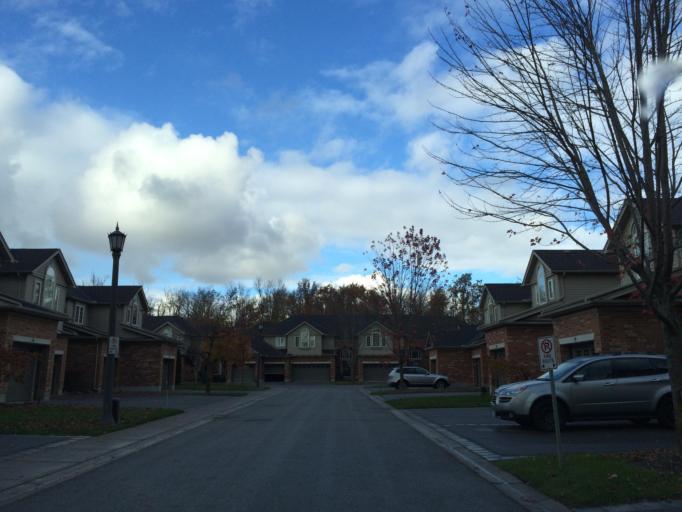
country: CA
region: Ontario
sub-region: Wellington County
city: Guelph
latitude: 43.5261
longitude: -80.3010
